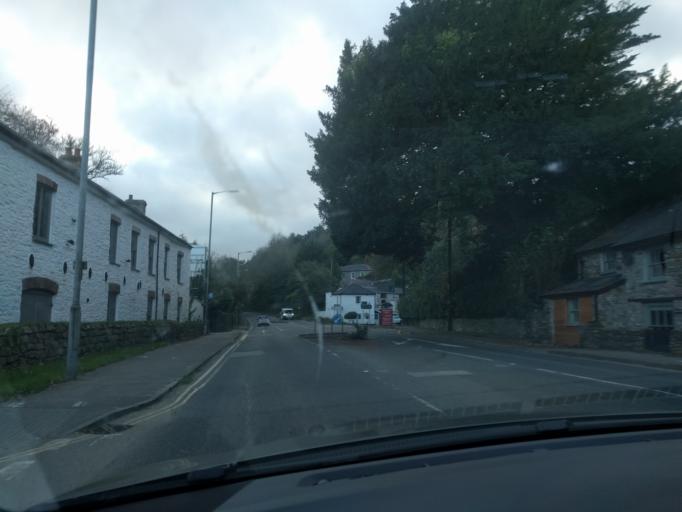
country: GB
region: England
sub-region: Cornwall
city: Perranarworthal
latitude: 50.2047
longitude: -5.1185
